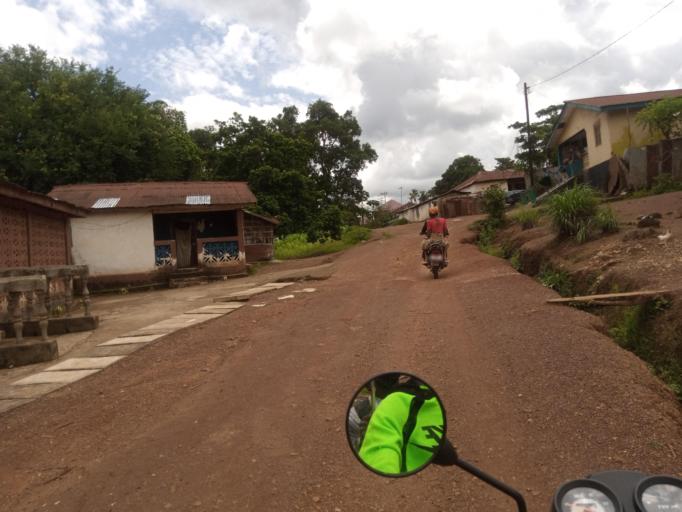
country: SL
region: Northern Province
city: Port Loko
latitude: 8.7629
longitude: -12.7838
